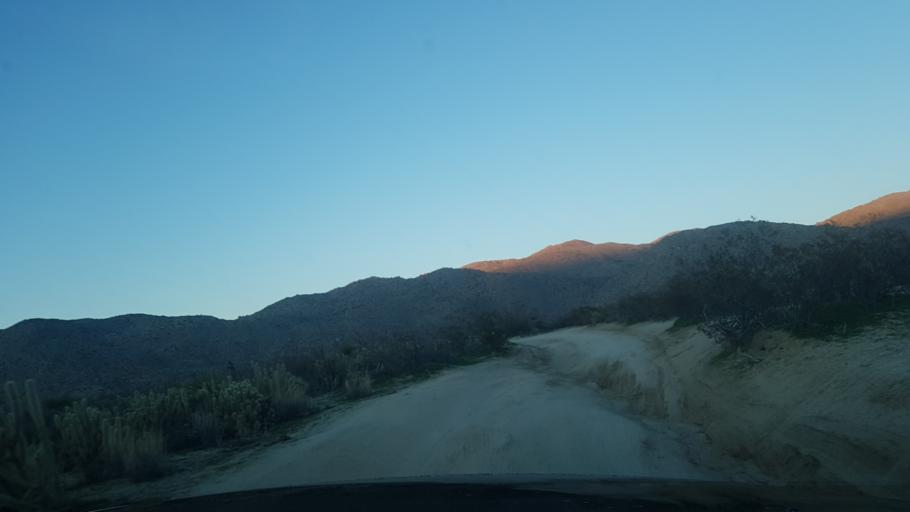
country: US
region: California
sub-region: San Diego County
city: Julian
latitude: 33.0151
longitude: -116.3739
